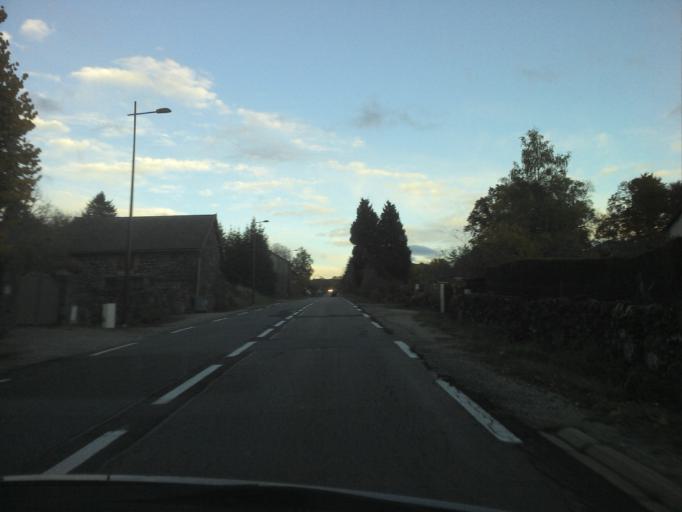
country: FR
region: Auvergne
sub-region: Departement du Puy-de-Dome
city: Saint-Ours
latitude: 45.8235
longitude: 2.9142
